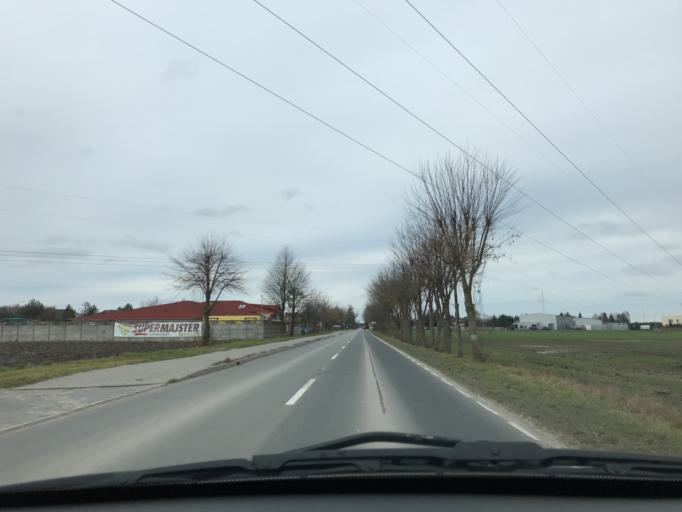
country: PL
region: Greater Poland Voivodeship
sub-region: Powiat poznanski
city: Baranowo
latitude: 52.3962
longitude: 16.7598
